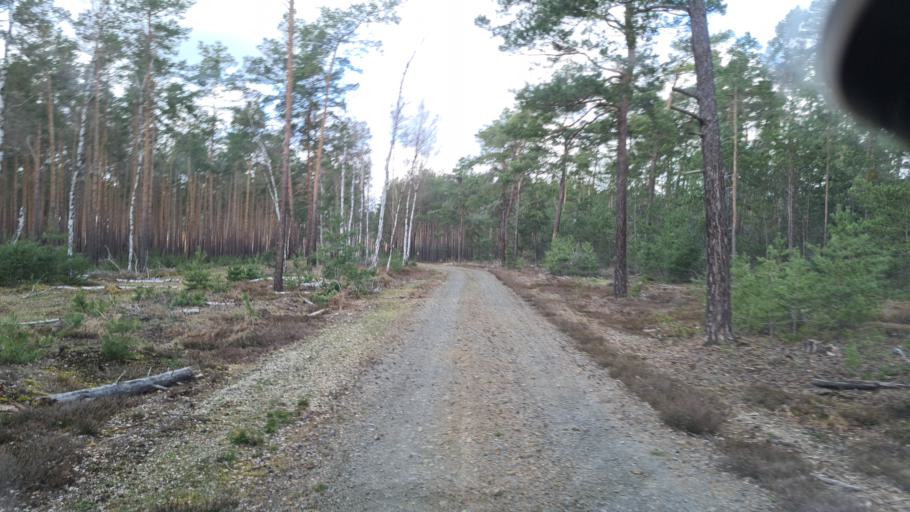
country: DE
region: Brandenburg
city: Schonborn
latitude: 51.6507
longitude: 13.4756
